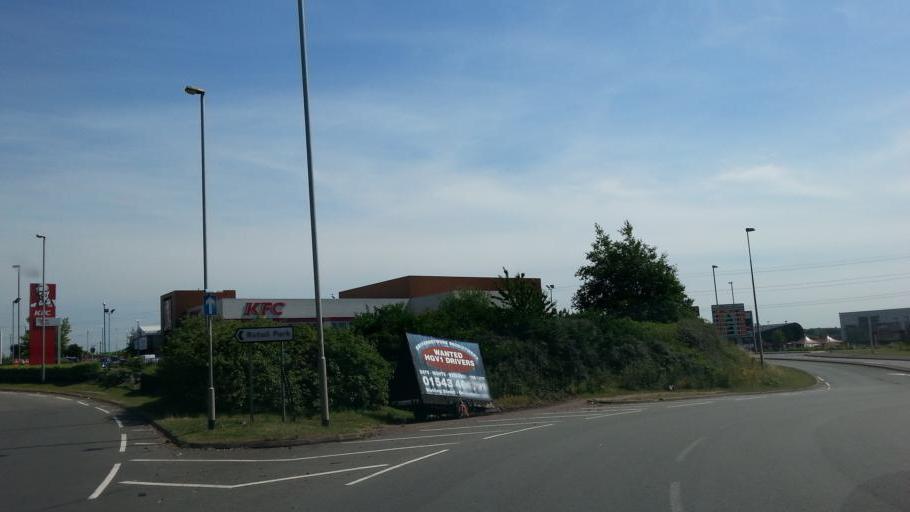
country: GB
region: England
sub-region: Staffordshire
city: Great Wyrley
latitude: 52.6750
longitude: -2.0212
